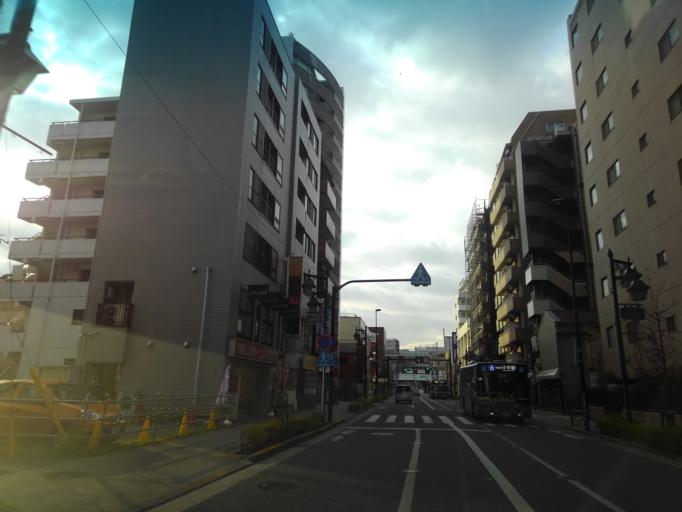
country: JP
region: Tokyo
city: Kokubunji
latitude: 35.7030
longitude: 139.5074
